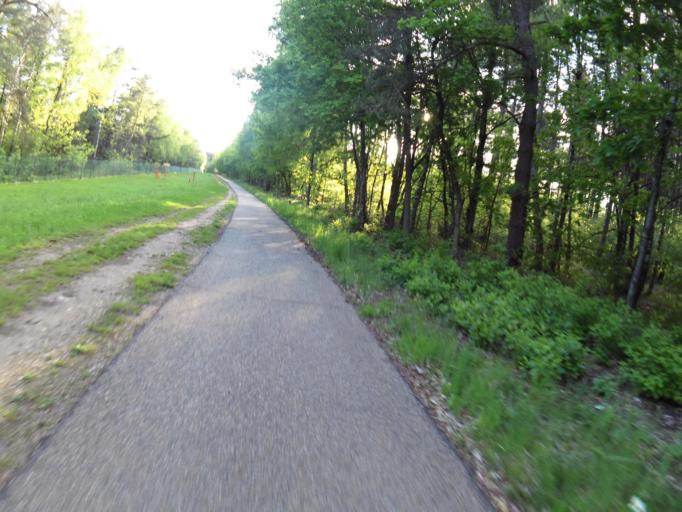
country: BE
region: Flanders
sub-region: Provincie Limburg
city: Zutendaal
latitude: 50.9519
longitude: 5.6267
